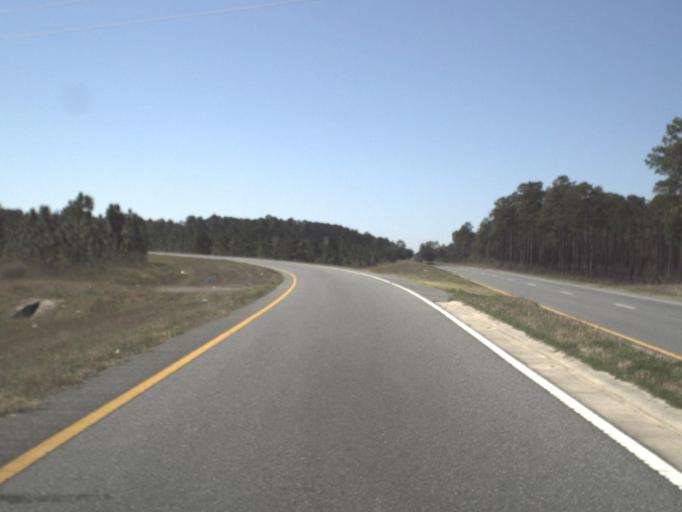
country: US
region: Florida
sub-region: Leon County
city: Woodville
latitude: 30.3500
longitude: -84.3098
